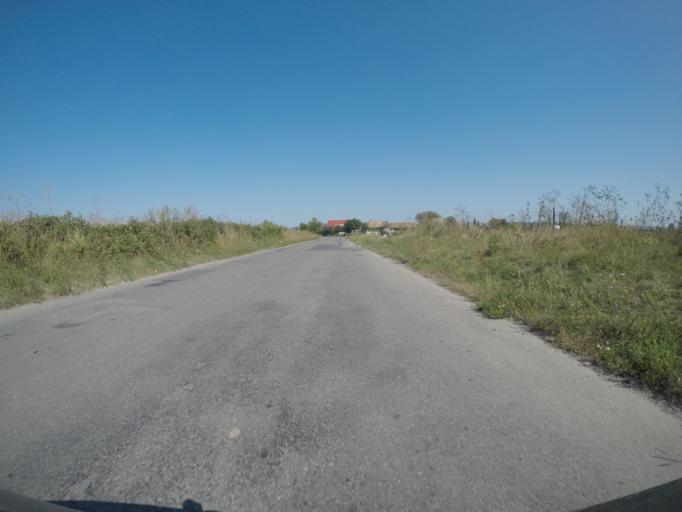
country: RO
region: Brasov
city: Fogarasch
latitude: 45.8230
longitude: 24.9797
